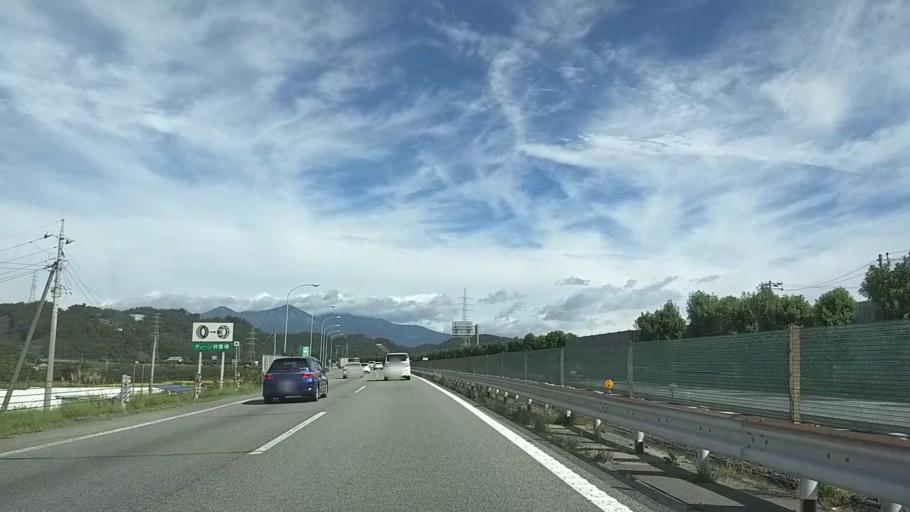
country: JP
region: Yamanashi
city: Nirasaki
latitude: 35.7781
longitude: 138.4224
